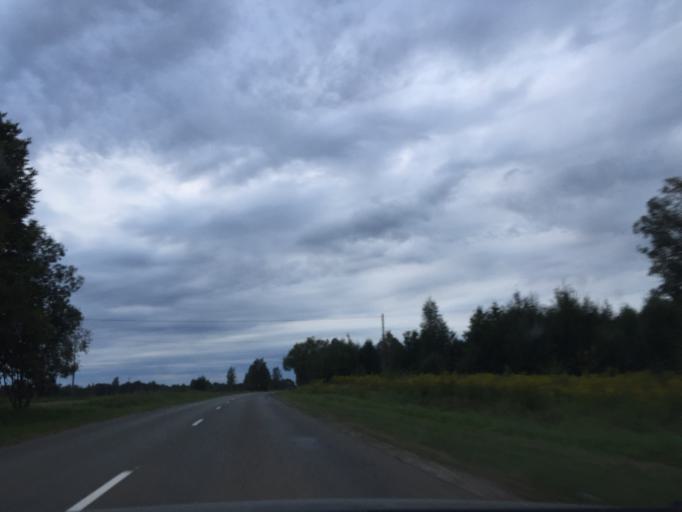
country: LV
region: Vecumnieki
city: Vecumnieki
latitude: 56.5096
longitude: 24.5640
